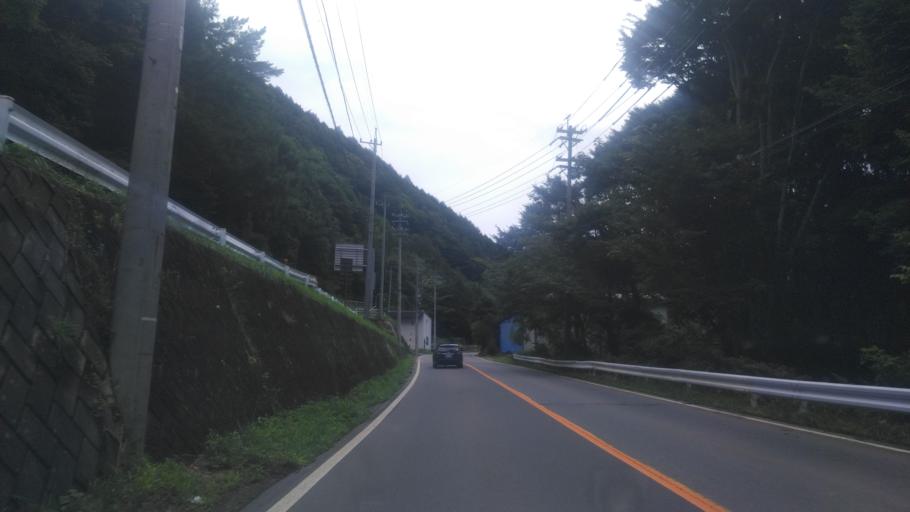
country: JP
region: Nagano
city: Ueda
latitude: 36.4900
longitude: 138.3601
